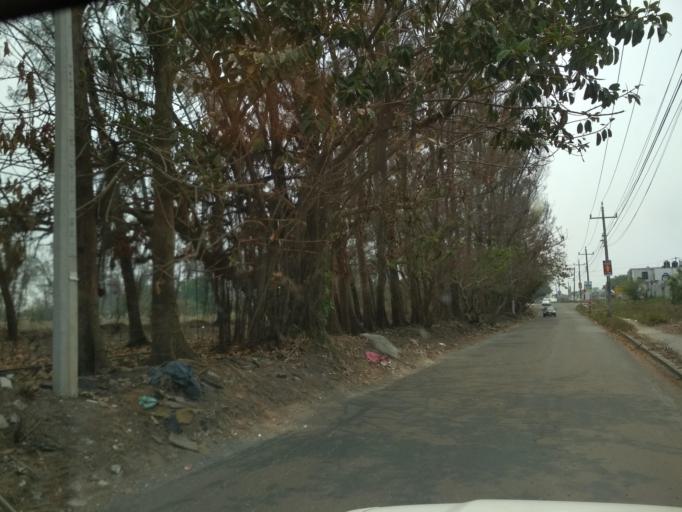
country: MX
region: Veracruz
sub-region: Veracruz
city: Las Amapolas
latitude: 19.1512
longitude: -96.2211
